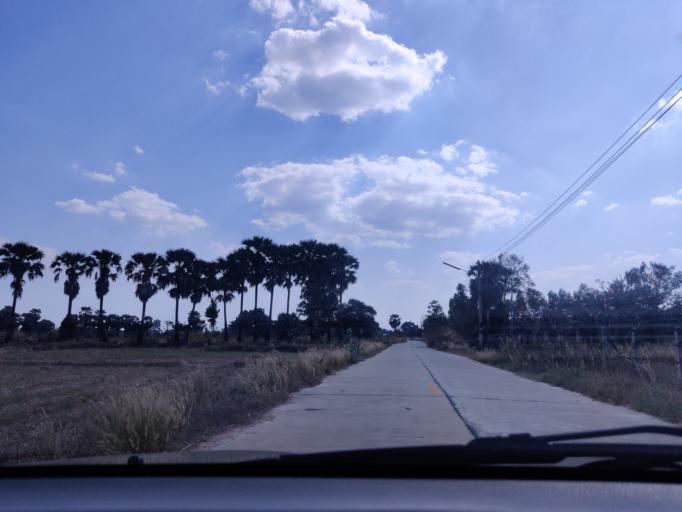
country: TH
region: Sisaket
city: Si Sa Ket
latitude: 15.0952
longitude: 104.3552
